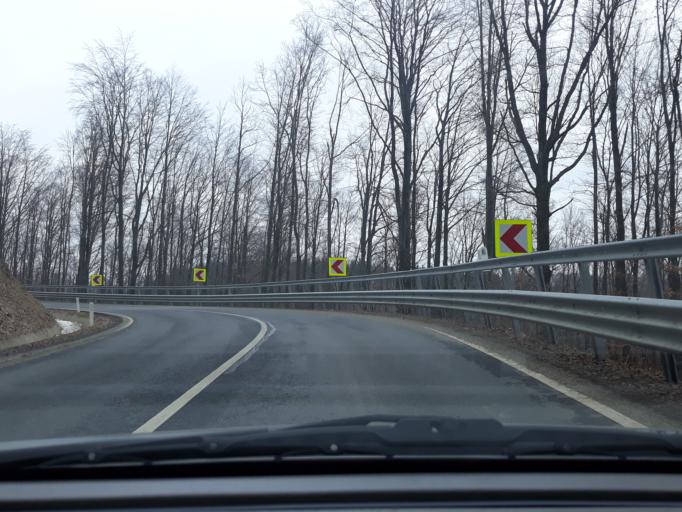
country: RO
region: Bihor
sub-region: Oras Alesd
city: Padurea Neagra
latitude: 47.1222
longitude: 22.4232
